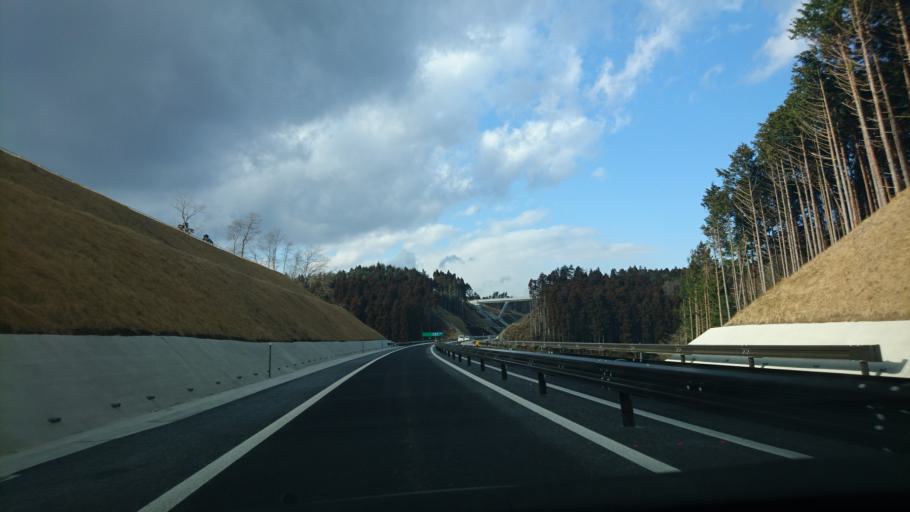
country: JP
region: Miyagi
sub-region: Oshika Gun
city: Onagawa Cho
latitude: 38.7632
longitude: 141.4977
